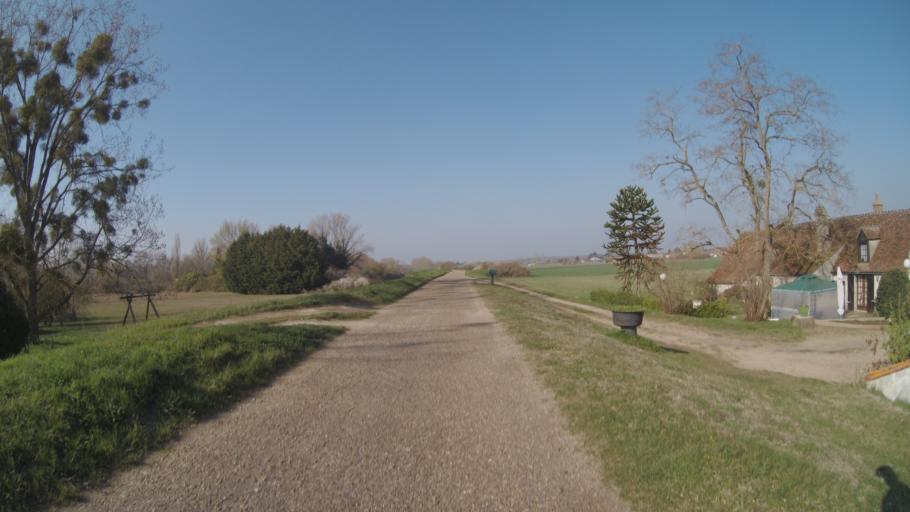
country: FR
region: Centre
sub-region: Departement du Loiret
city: Sandillon
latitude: 47.8686
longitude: 2.0369
